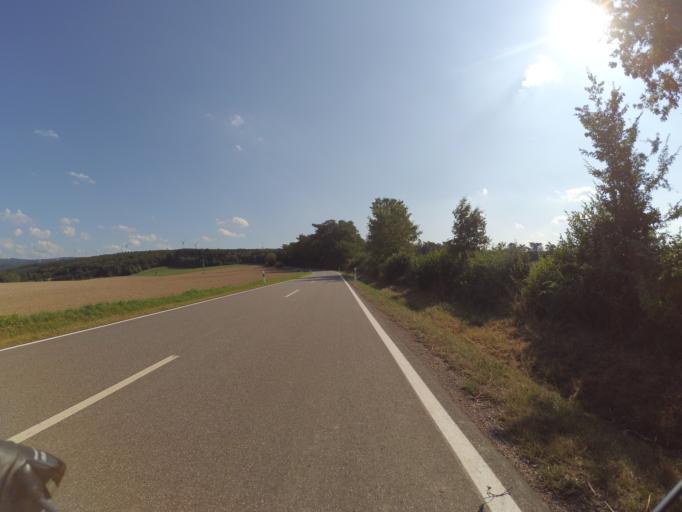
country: DE
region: Rheinland-Pfalz
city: Wintrich
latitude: 49.8698
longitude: 6.9625
